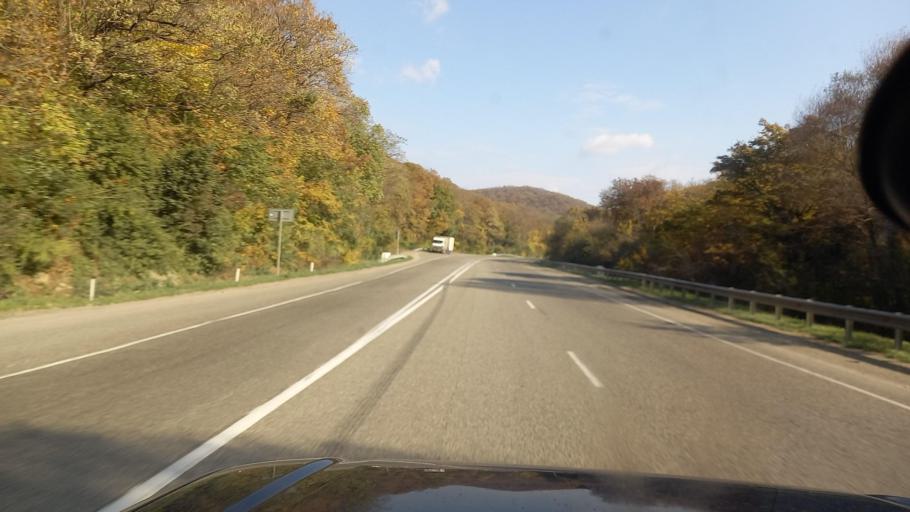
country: RU
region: Krasnodarskiy
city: Verkhnebakanskiy
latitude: 44.8457
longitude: 37.7190
